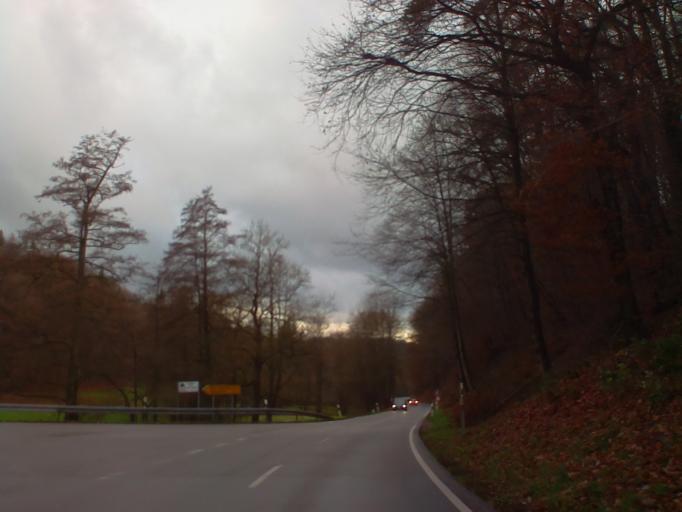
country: DE
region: Hesse
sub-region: Regierungsbezirk Darmstadt
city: Wald-Michelbach
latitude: 49.5747
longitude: 8.7869
